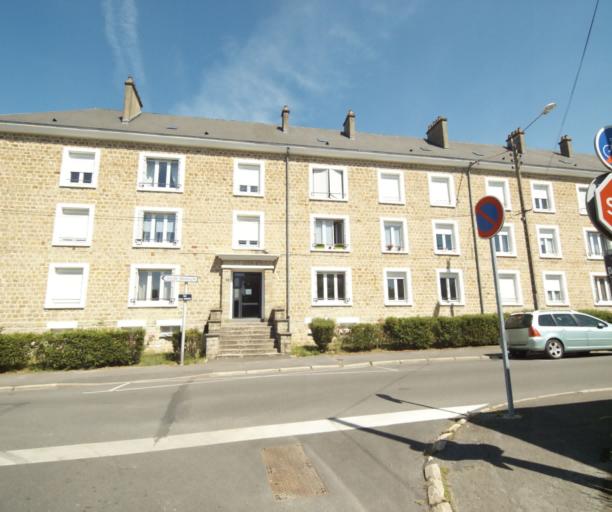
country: FR
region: Champagne-Ardenne
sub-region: Departement des Ardennes
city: Charleville-Mezieres
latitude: 49.7525
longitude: 4.7221
